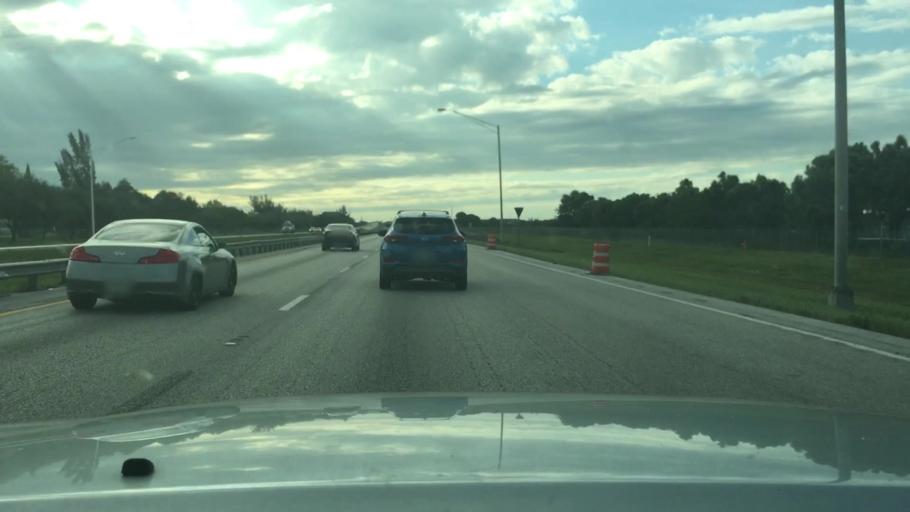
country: US
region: Florida
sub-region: Miami-Dade County
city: Lake Lucerne
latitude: 25.9733
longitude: -80.2548
